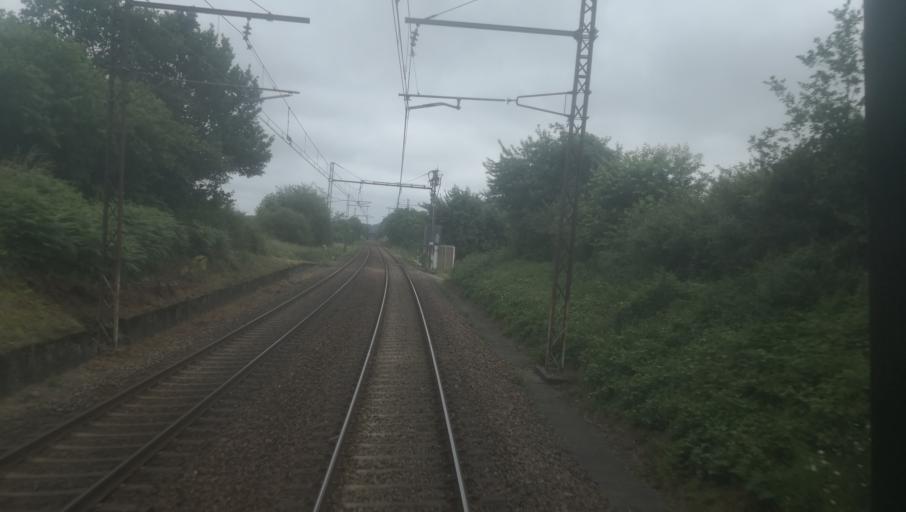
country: FR
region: Limousin
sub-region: Departement de la Creuse
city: La Souterraine
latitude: 46.2009
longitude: 1.4753
